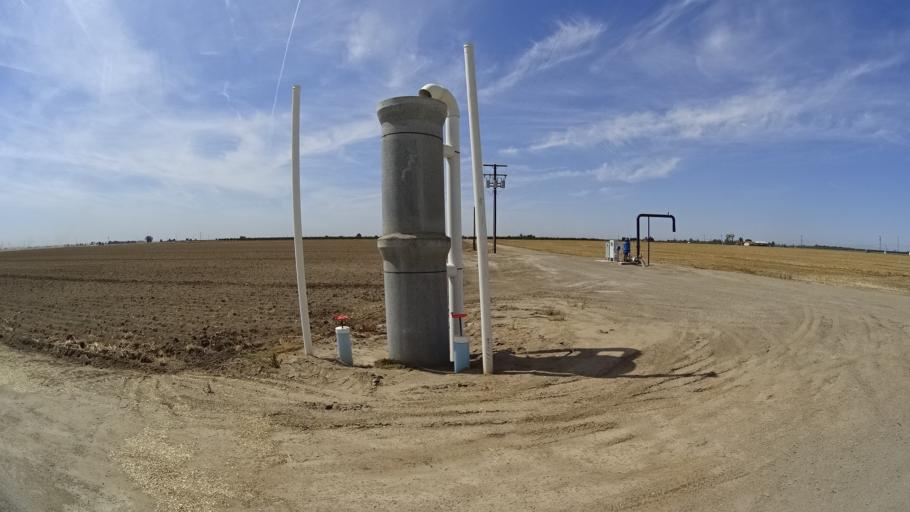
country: US
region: California
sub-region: Kings County
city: Hanford
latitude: 36.3574
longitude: -119.5617
